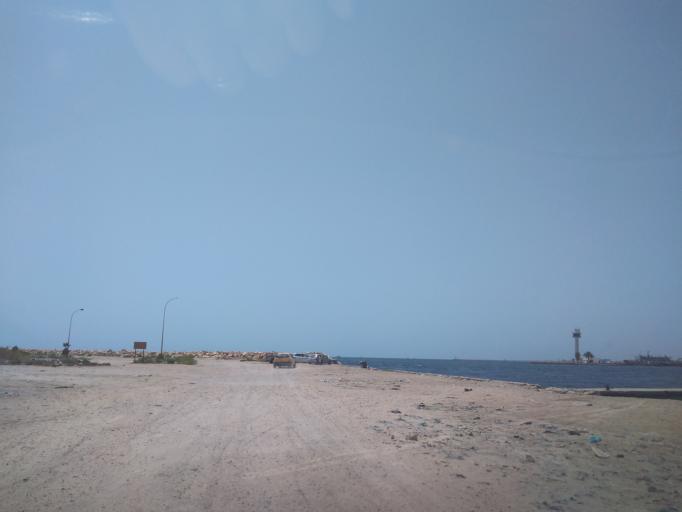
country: TN
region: Safaqis
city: Sfax
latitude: 34.7246
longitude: 10.7792
